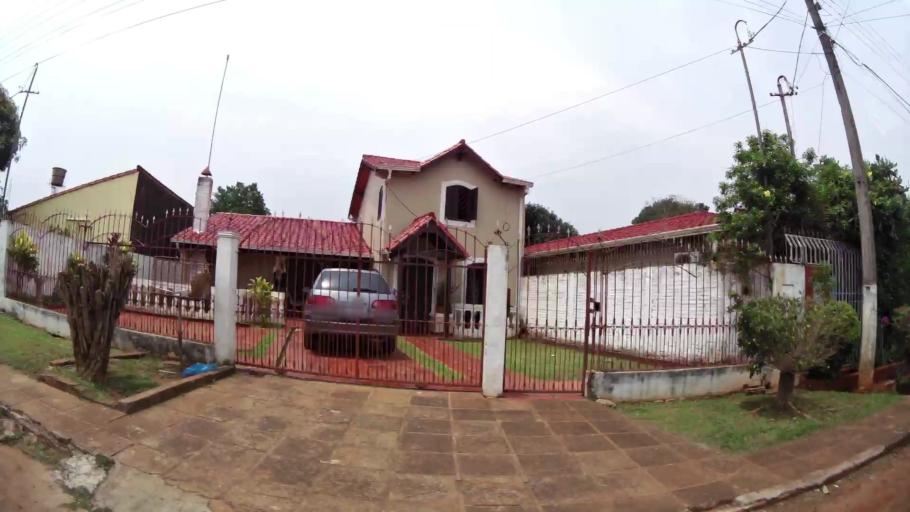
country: PY
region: Alto Parana
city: Presidente Franco
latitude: -25.5557
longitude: -54.6243
